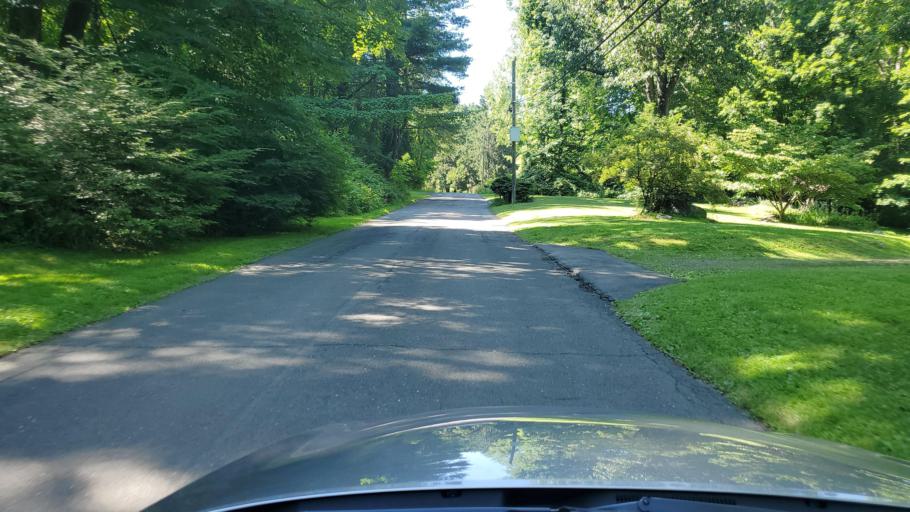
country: US
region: Connecticut
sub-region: Fairfield County
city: Westport
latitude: 41.2186
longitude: -73.3333
